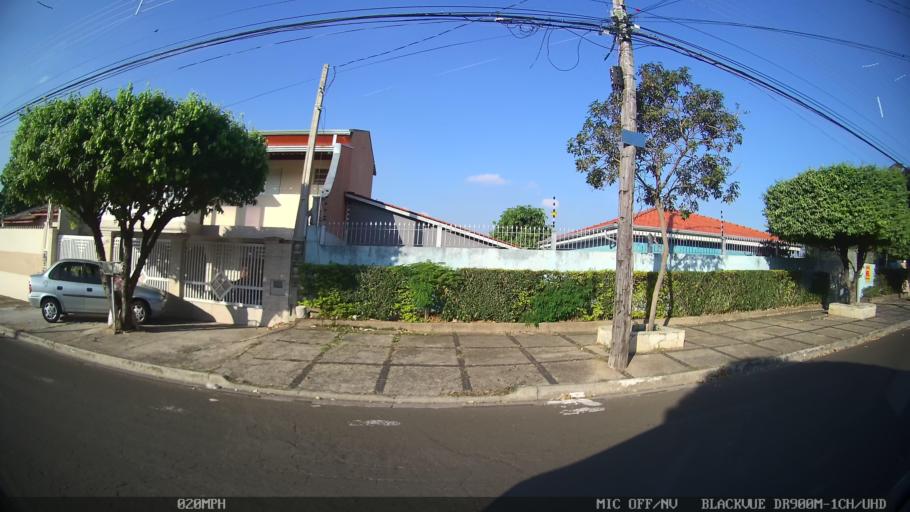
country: BR
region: Sao Paulo
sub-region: Campinas
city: Campinas
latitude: -22.9667
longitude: -47.1256
